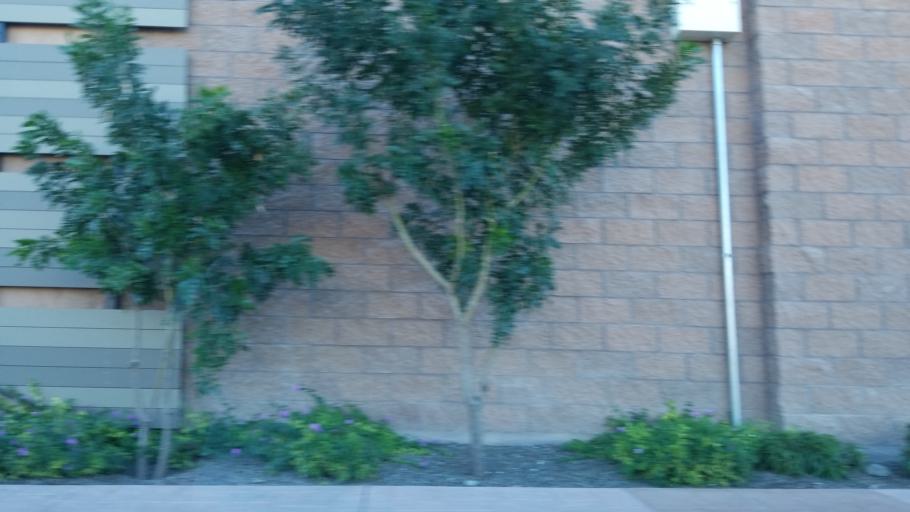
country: US
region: Arizona
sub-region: Maricopa County
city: Paradise Valley
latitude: 33.5286
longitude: -111.9266
